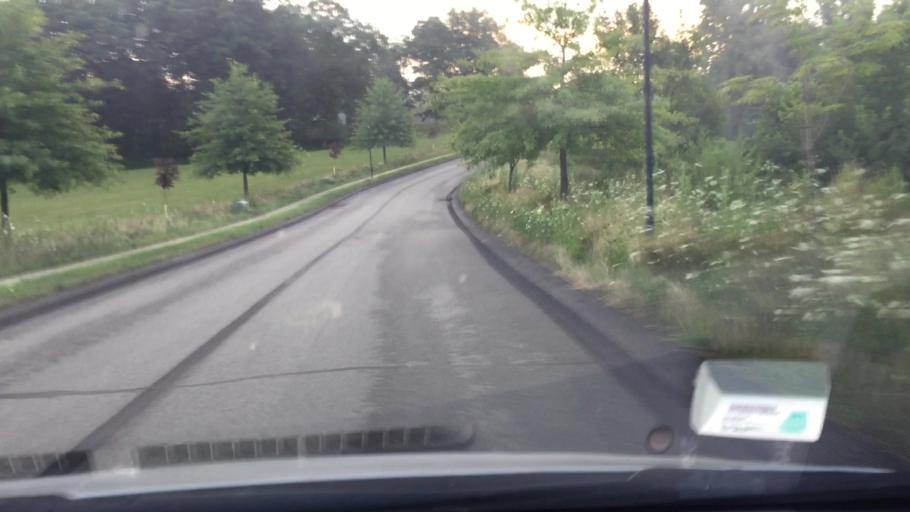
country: US
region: Pennsylvania
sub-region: Allegheny County
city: Allison Park
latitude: 40.5433
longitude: -79.9328
